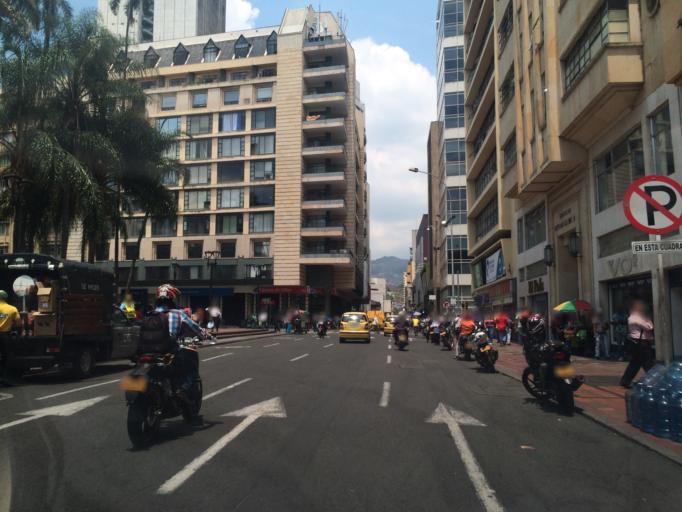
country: CO
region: Valle del Cauca
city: Cali
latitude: 3.4523
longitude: -76.5324
